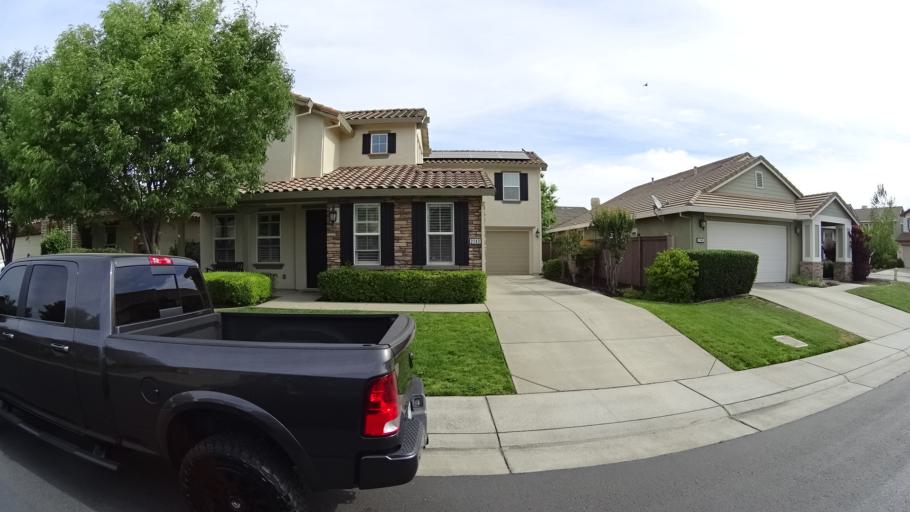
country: US
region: California
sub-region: Placer County
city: Lincoln
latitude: 38.8355
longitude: -121.2764
